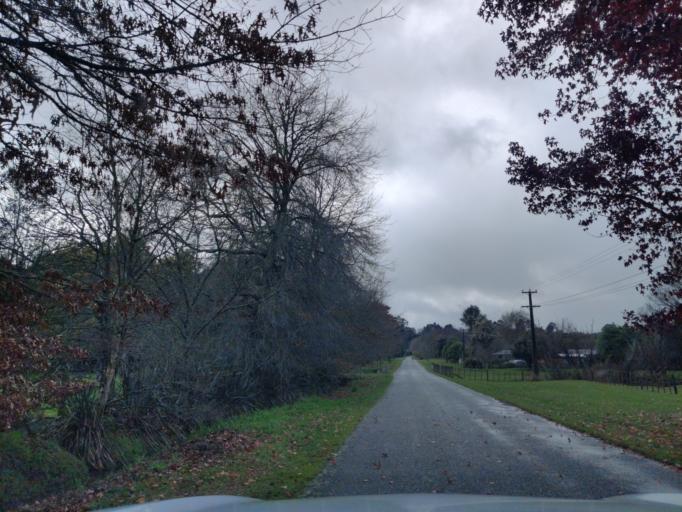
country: NZ
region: Manawatu-Wanganui
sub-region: Palmerston North City
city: Palmerston North
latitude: -40.1724
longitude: 175.7963
